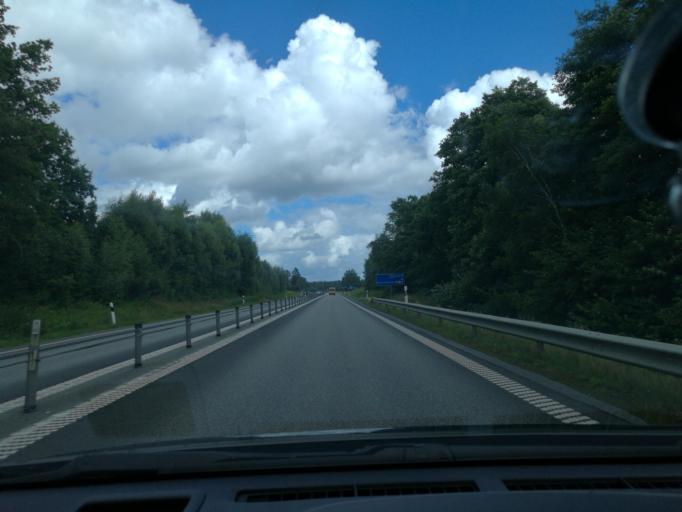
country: SE
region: Skane
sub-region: Hassleholms Kommun
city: Hastveda
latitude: 56.2151
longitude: 13.8760
